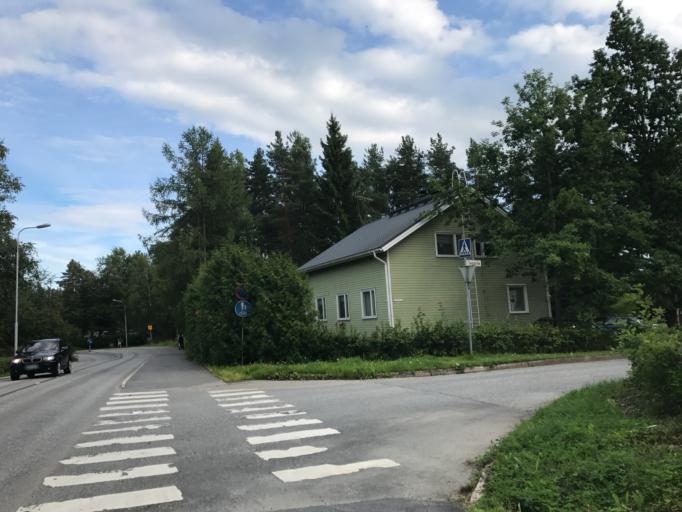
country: FI
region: Pirkanmaa
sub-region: Etelae-Pirkanmaa
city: Valkeakoski
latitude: 61.2509
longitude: 24.0516
